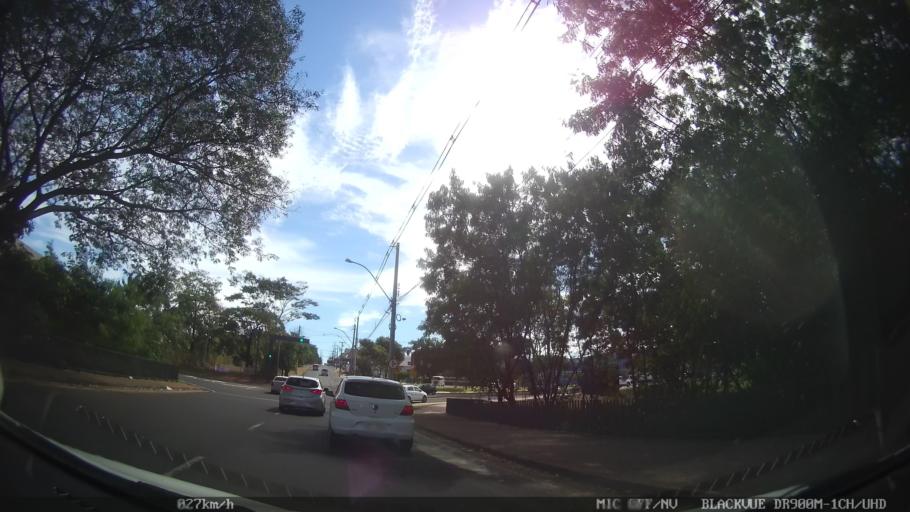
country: BR
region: Sao Paulo
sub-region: Sao Jose Do Rio Preto
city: Sao Jose do Rio Preto
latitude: -20.8413
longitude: -49.3517
